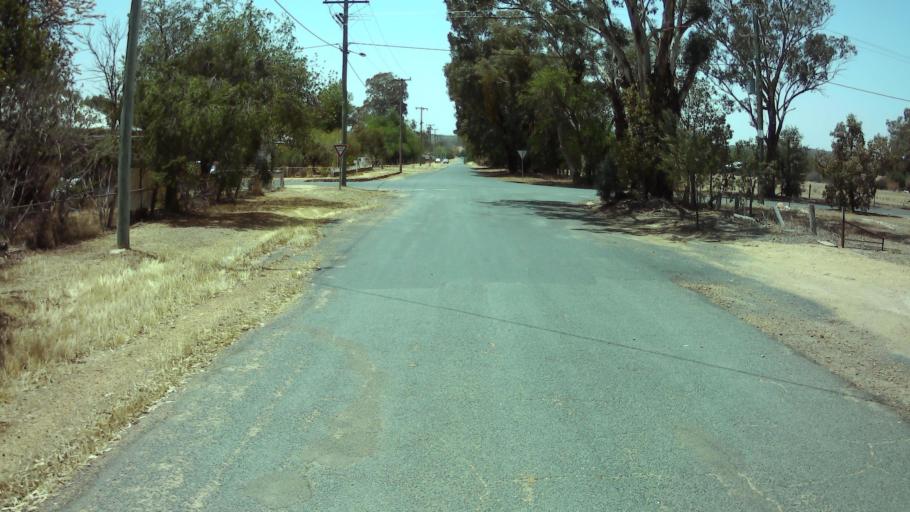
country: AU
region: New South Wales
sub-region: Weddin
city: Grenfell
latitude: -33.8891
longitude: 148.1513
